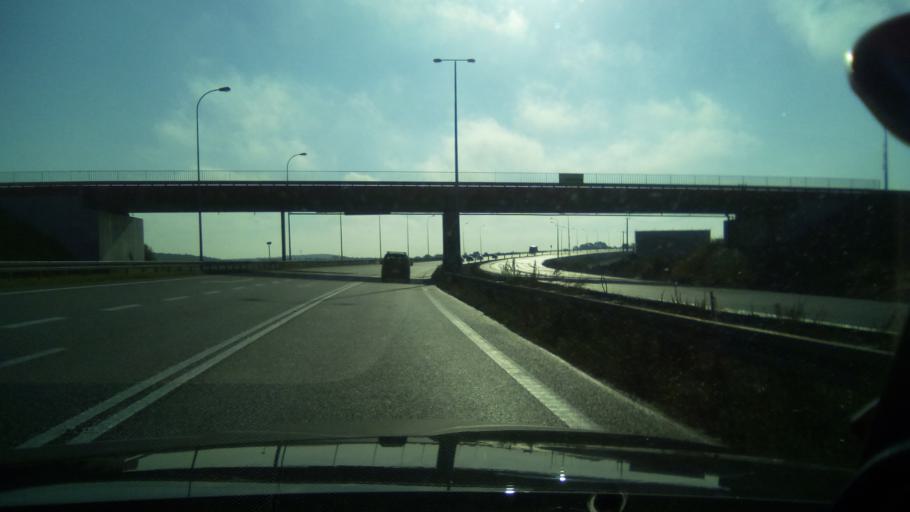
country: PL
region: Silesian Voivodeship
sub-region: Powiat bedzinski
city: Mierzecice
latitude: 50.4504
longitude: 19.1283
